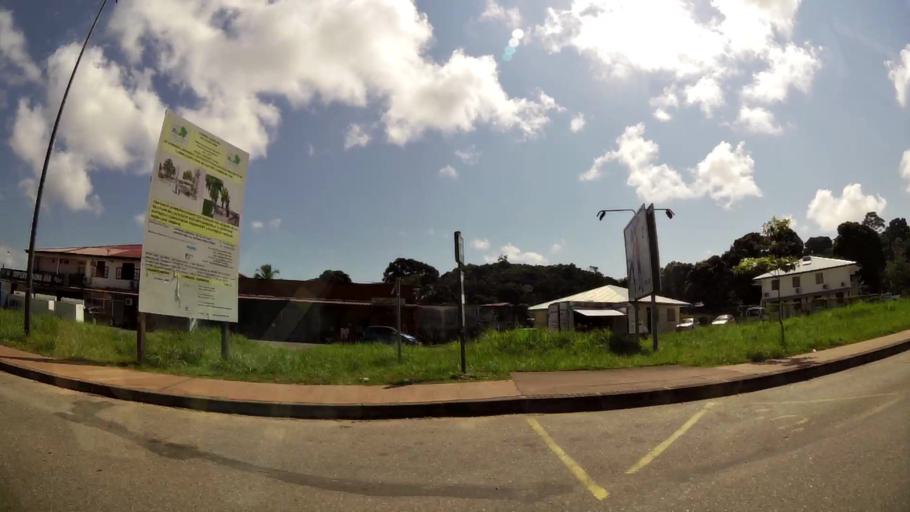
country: GF
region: Guyane
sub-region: Guyane
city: Cayenne
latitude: 4.9173
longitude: -52.3125
